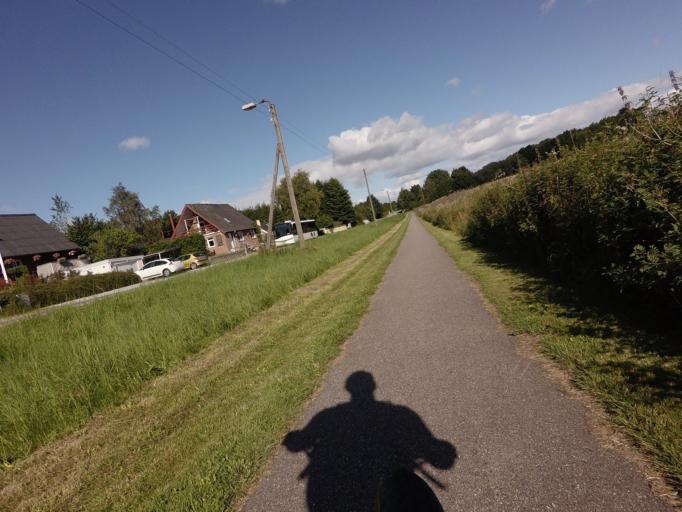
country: DK
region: Central Jutland
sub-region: Skanderborg Kommune
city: Ry
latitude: 55.9724
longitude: 9.7419
